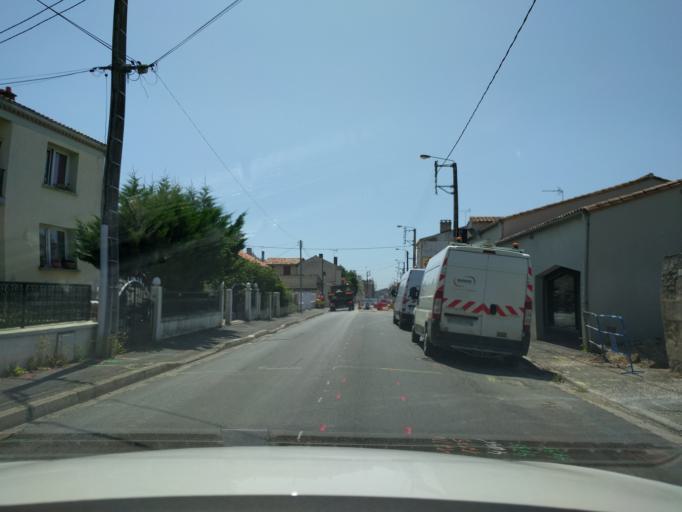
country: FR
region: Poitou-Charentes
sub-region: Departement des Deux-Sevres
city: Niort
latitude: 46.3402
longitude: -0.4741
